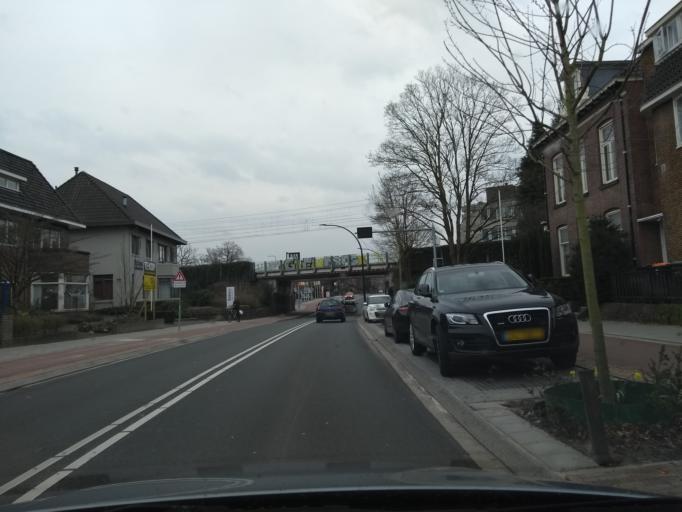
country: NL
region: Overijssel
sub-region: Gemeente Hengelo
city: Hengelo
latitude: 52.2624
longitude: 6.8011
